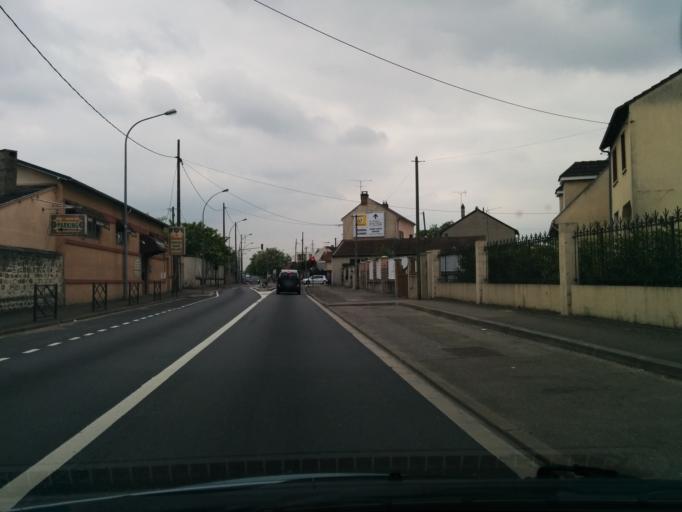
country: FR
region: Ile-de-France
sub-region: Departement des Yvelines
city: Les Mureaux
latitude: 48.9898
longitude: 1.8992
